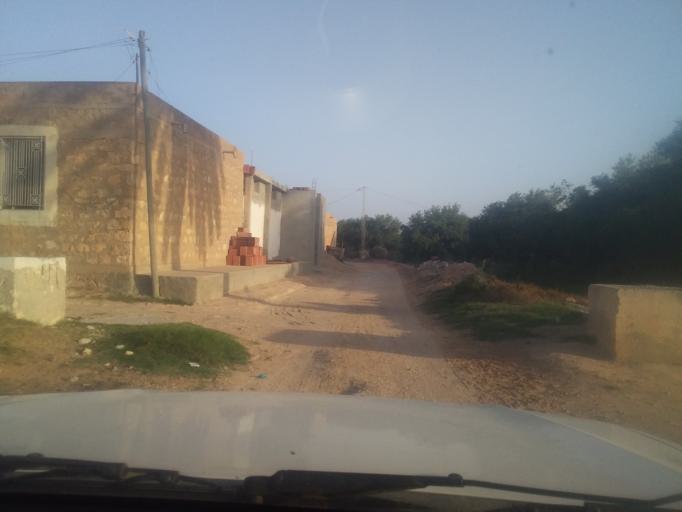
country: TN
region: Qabis
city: Gabes
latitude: 33.6319
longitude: 10.2935
